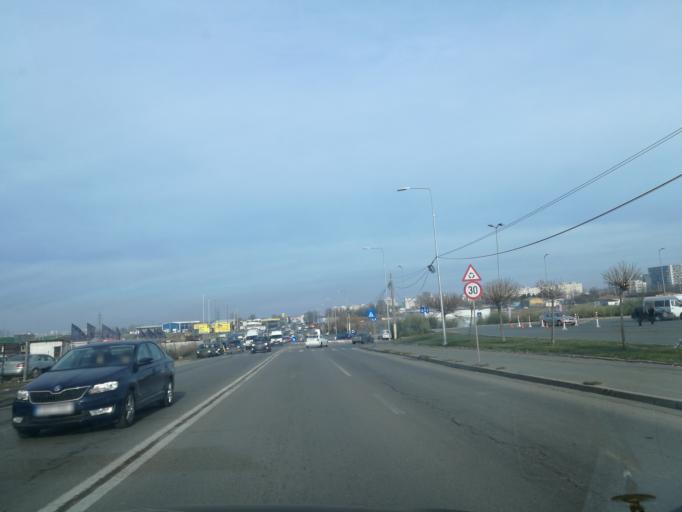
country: RO
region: Constanta
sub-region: Municipiul Constanta
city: Palazu Mare
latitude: 44.2006
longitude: 28.6077
